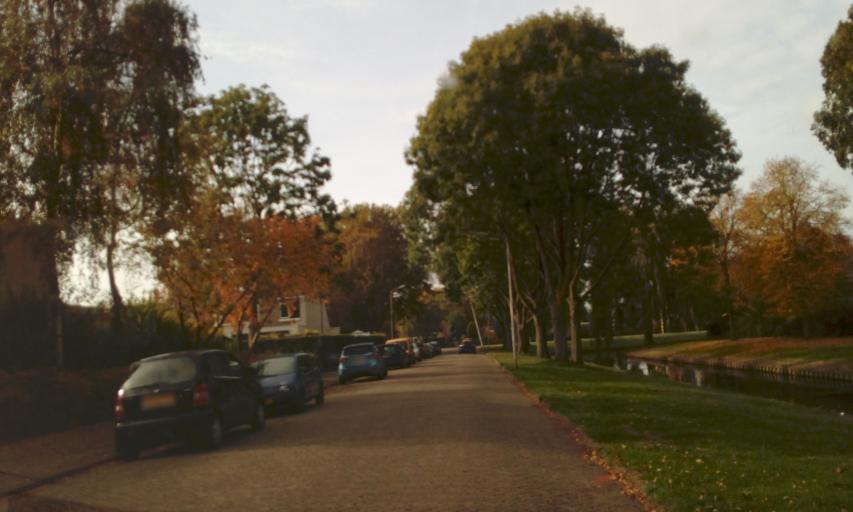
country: NL
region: South Holland
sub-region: Gemeente Lansingerland
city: Bergschenhoek
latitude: 52.0041
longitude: 4.4935
